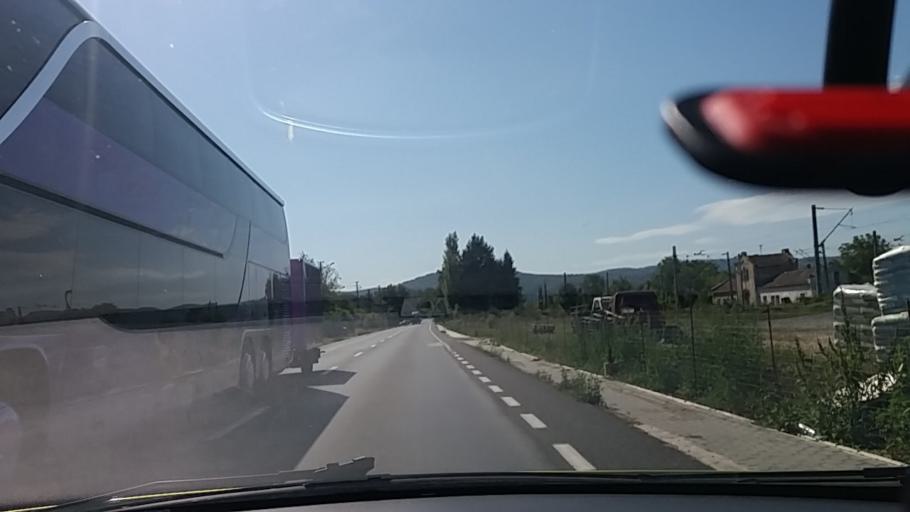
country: RO
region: Hunedoara
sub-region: Comuna Zam
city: Zam
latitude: 46.0027
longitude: 22.4417
